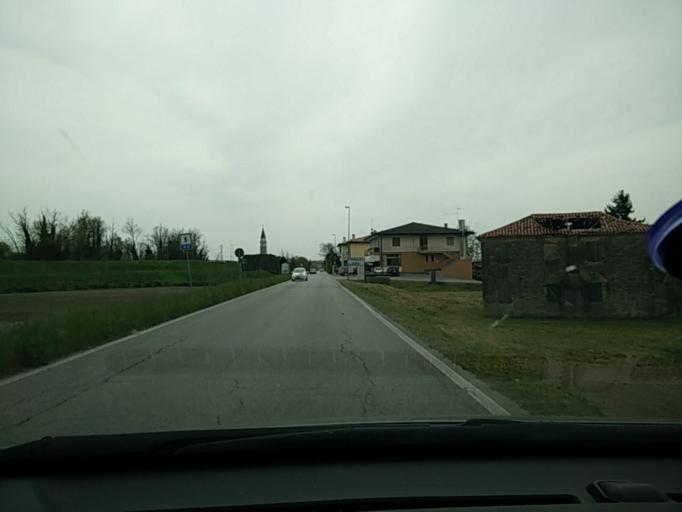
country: IT
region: Veneto
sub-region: Provincia di Venezia
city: Fossalta di Piave
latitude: 45.6534
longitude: 12.5116
